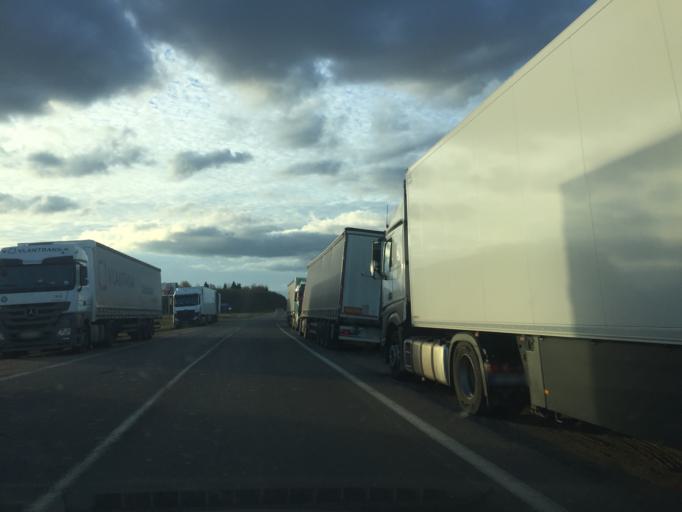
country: BY
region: Vitebsk
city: Myory
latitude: 55.8160
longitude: 27.6644
